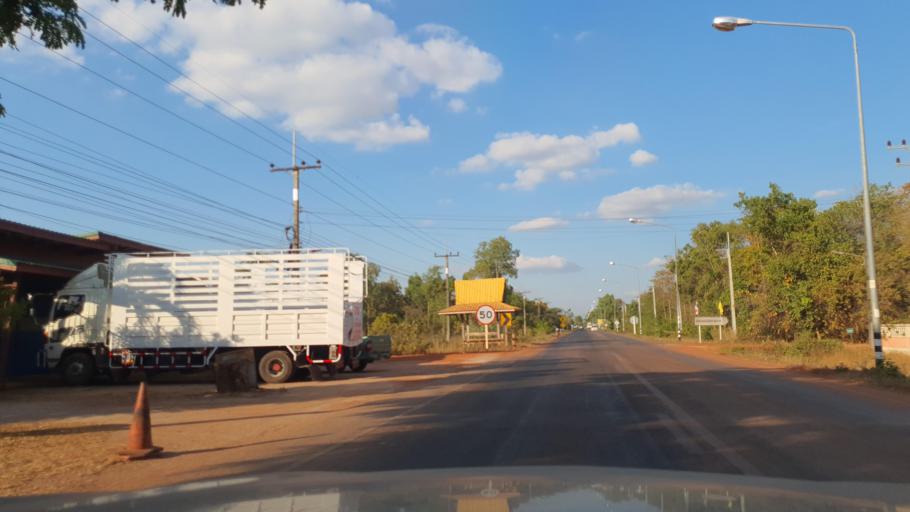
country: TH
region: Sakon Nakhon
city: Phon Na Kaeo
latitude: 17.2707
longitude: 104.1916
